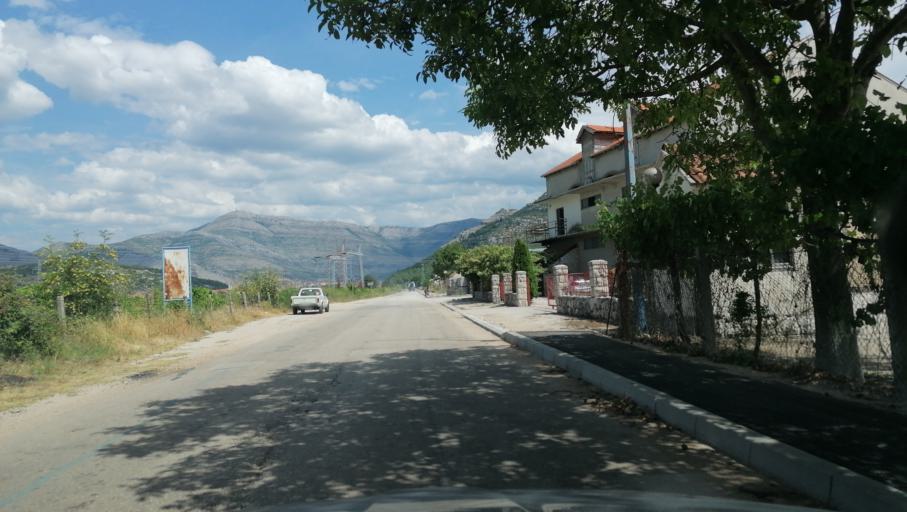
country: BA
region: Republika Srpska
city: Trebinje
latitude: 42.6743
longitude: 18.3301
